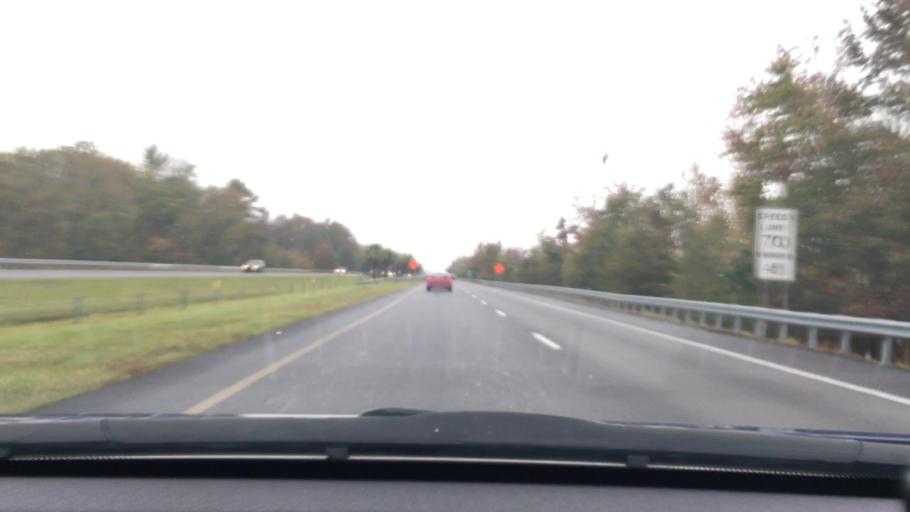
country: US
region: South Carolina
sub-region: Lee County
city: Bishopville
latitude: 34.1887
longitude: -80.1796
